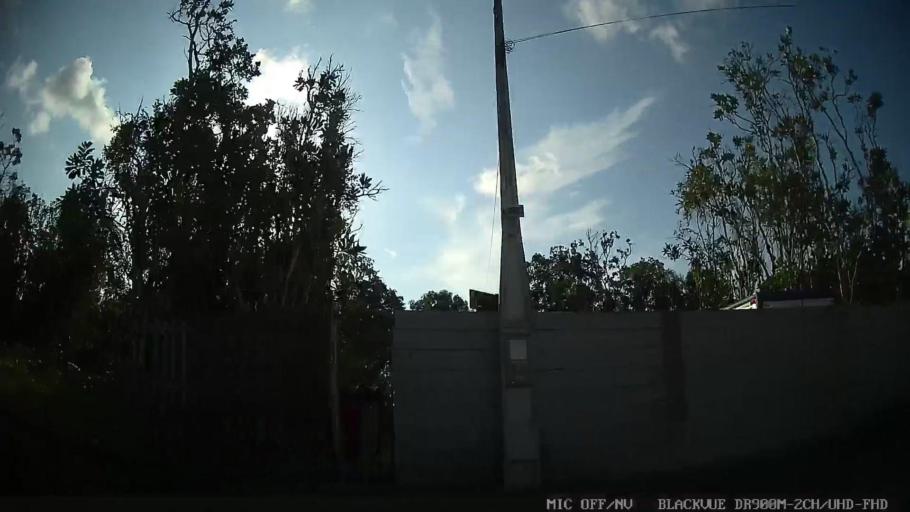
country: BR
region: Sao Paulo
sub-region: Itanhaem
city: Itanhaem
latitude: -24.1735
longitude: -46.8204
